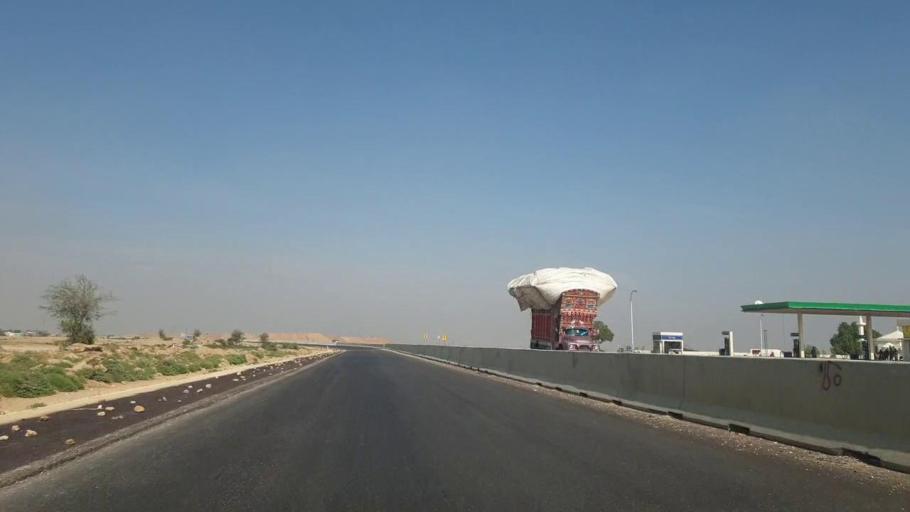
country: PK
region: Sindh
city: Jamshoro
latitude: 25.5707
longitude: 68.3139
